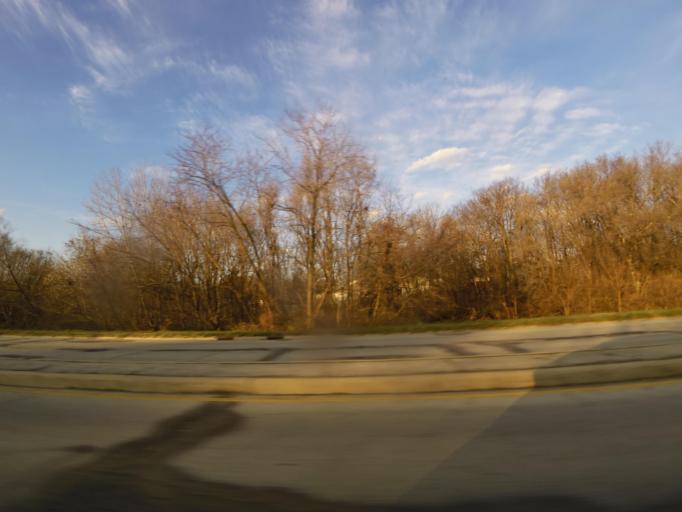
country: US
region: Illinois
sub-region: Fayette County
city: Vandalia
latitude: 38.9671
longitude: -89.0932
